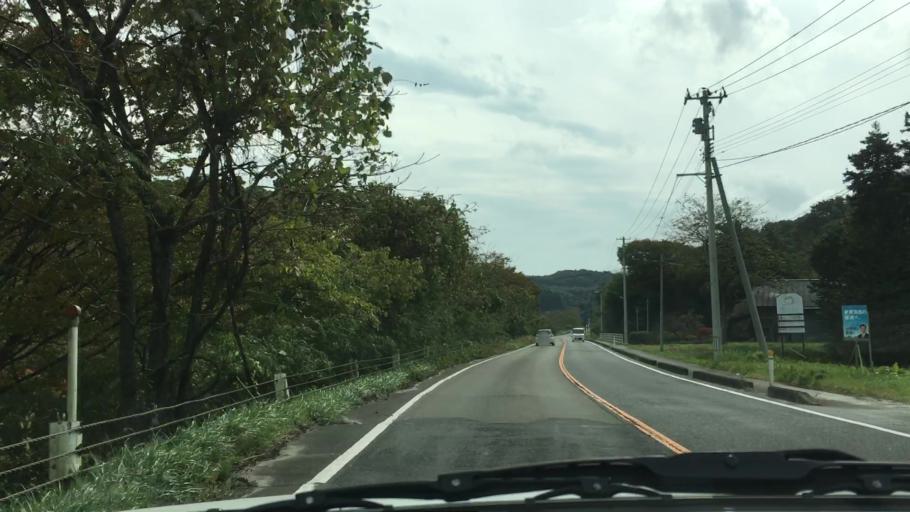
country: JP
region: Miyagi
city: Matsushima
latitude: 38.4265
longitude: 141.0606
